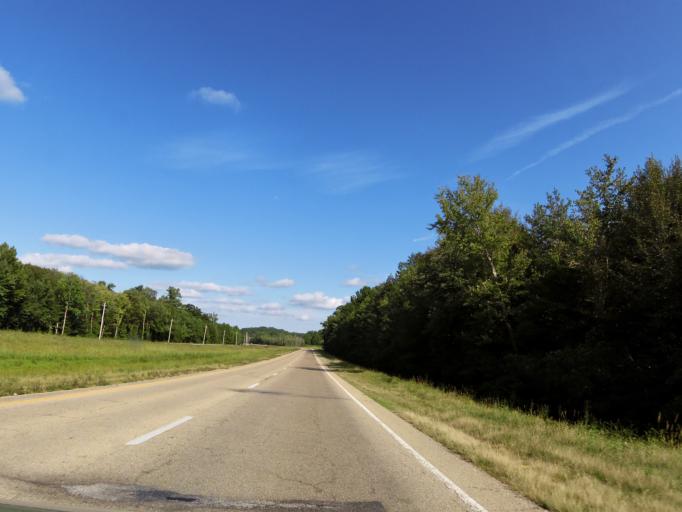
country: US
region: Mississippi
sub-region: Alcorn County
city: Farmington
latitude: 34.8580
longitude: -88.3942
